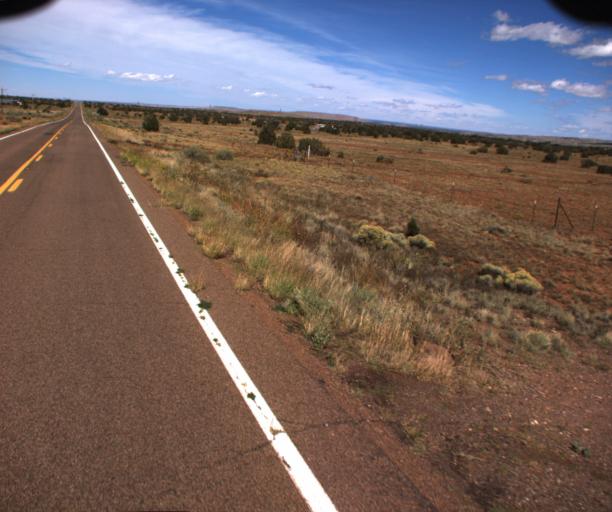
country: US
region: Arizona
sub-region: Apache County
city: Saint Johns
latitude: 34.5140
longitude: -109.6208
